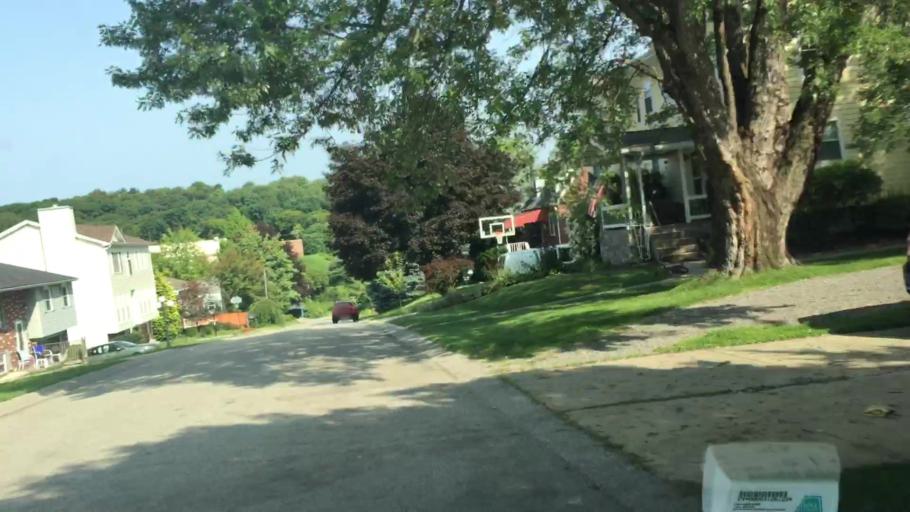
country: US
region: Pennsylvania
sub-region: Allegheny County
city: Blawnox
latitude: 40.5033
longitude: -79.8574
